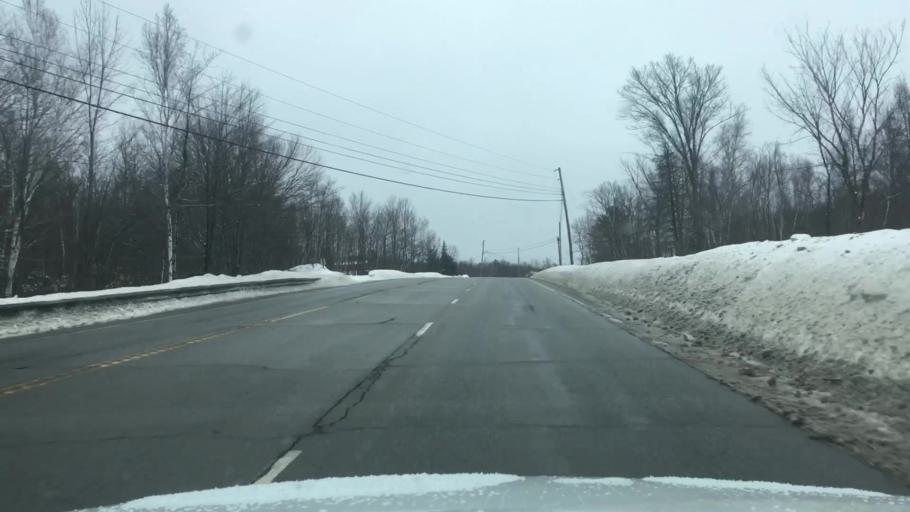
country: US
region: Maine
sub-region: Oxford County
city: Peru
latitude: 44.5818
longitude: -70.3695
